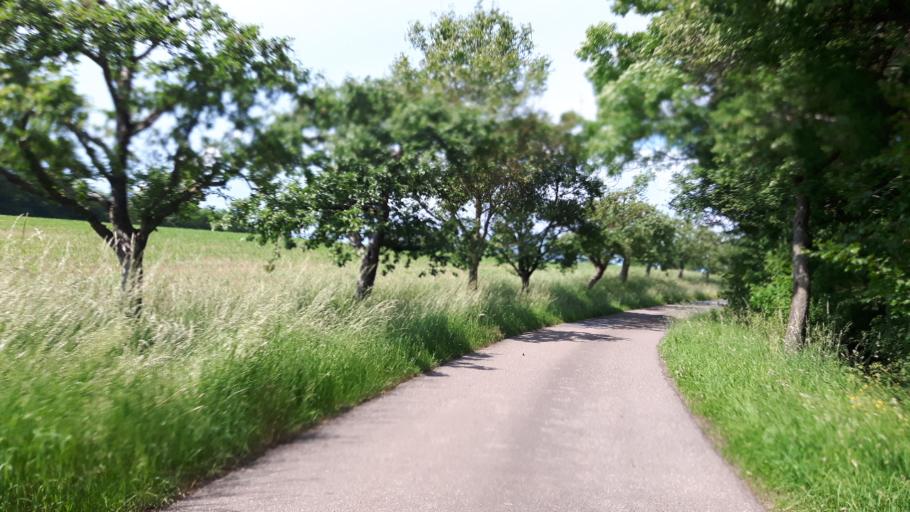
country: DE
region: Baden-Wuerttemberg
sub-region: Regierungsbezirk Stuttgart
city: Forchtenberg
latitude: 49.3340
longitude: 9.5272
